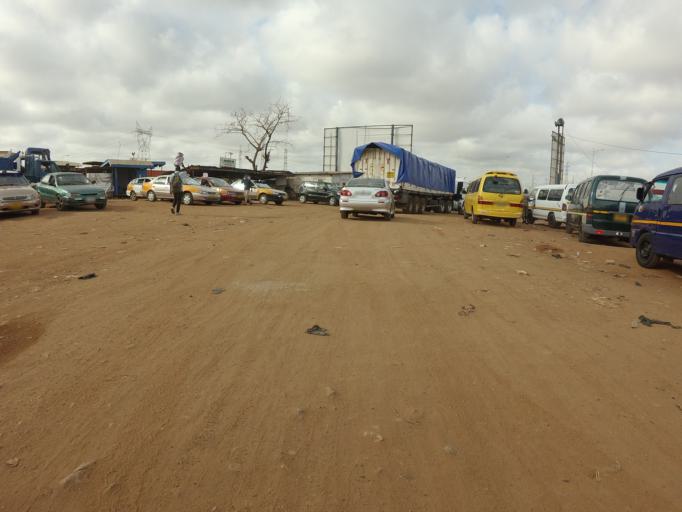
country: GH
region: Greater Accra
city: Tema
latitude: 5.6757
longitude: -0.0439
